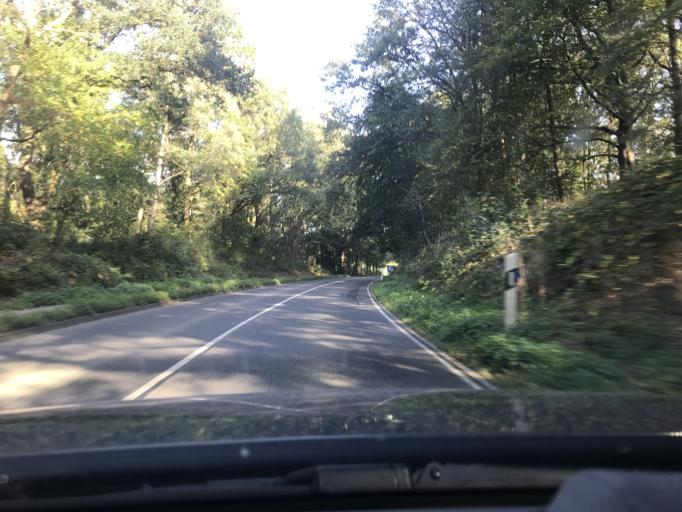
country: DE
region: North Rhine-Westphalia
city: Kalkar
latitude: 51.7415
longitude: 6.2509
